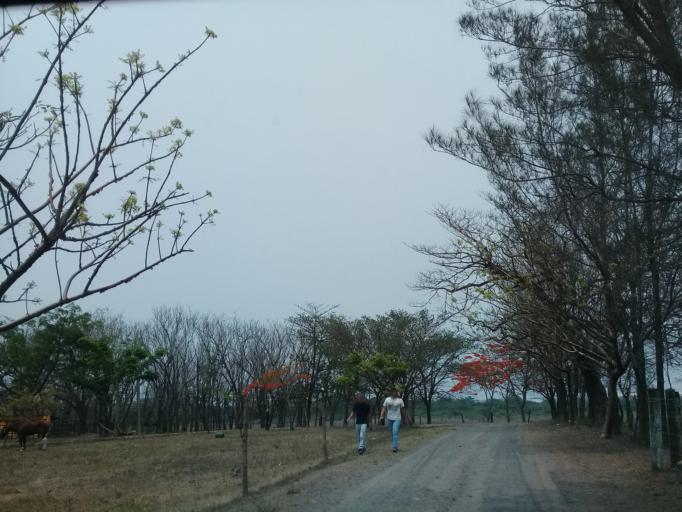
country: MX
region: Veracruz
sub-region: Veracruz
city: Lomas de Rio Medio Cuatro
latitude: 19.1726
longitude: -96.2111
